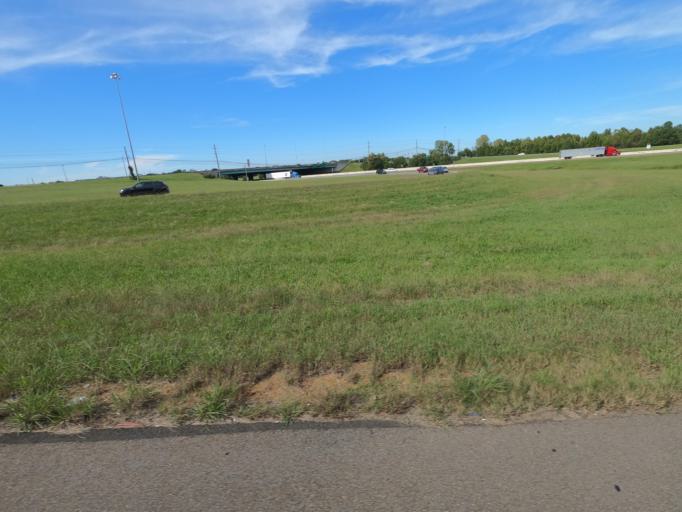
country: US
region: Tennessee
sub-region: Shelby County
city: Lakeland
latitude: 35.1940
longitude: -89.7902
